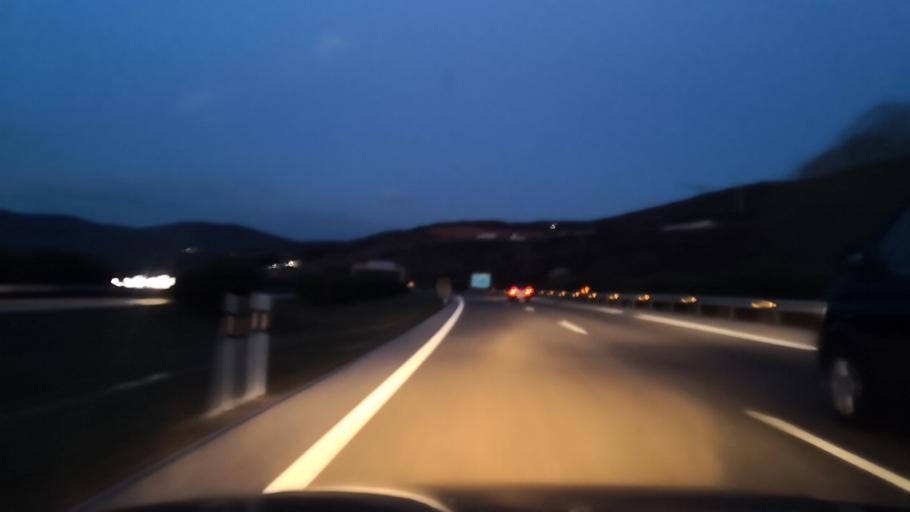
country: ES
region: Castille and Leon
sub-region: Provincia de Leon
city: Torre del Bierzo
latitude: 42.6069
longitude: -6.3526
